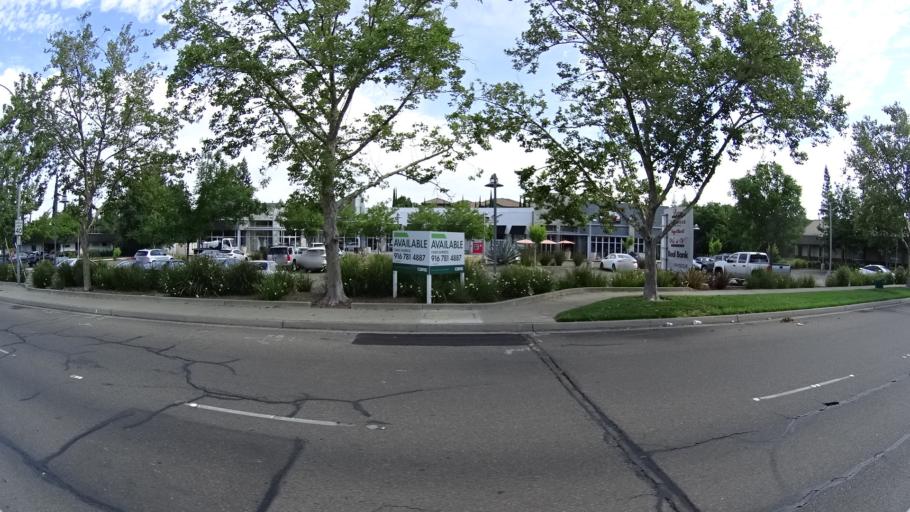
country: US
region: California
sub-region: Sacramento County
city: Arden-Arcade
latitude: 38.5743
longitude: -121.4066
